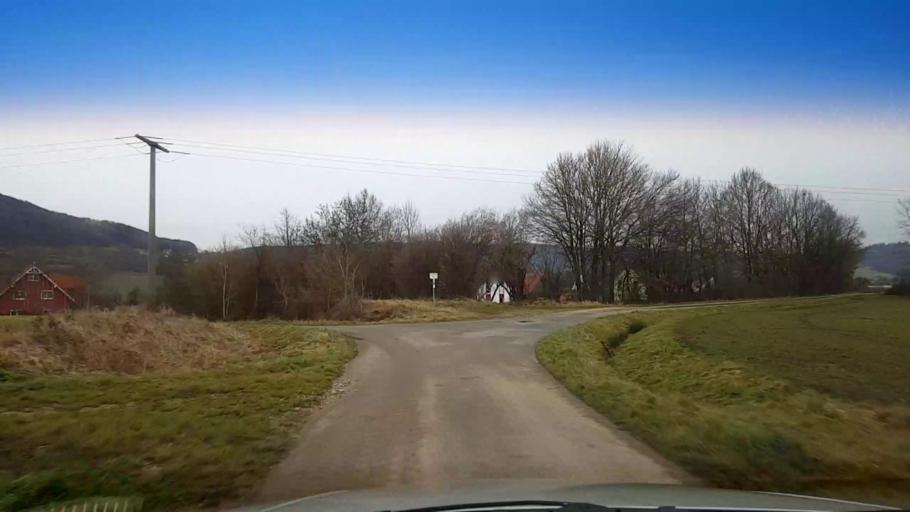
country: DE
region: Bavaria
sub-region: Upper Franconia
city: Schesslitz
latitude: 49.9935
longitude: 11.0424
